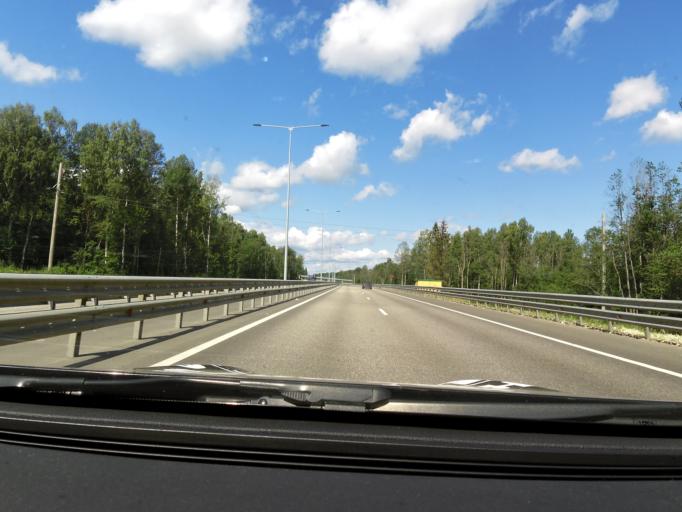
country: RU
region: Tverskaya
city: Vydropuzhsk
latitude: 57.3584
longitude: 34.6876
